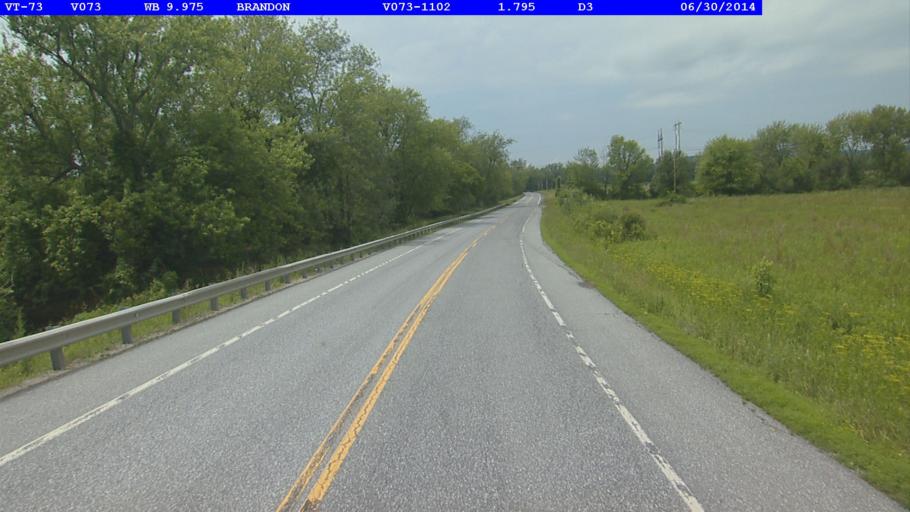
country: US
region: Vermont
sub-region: Rutland County
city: Brandon
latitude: 43.7994
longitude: -73.1170
